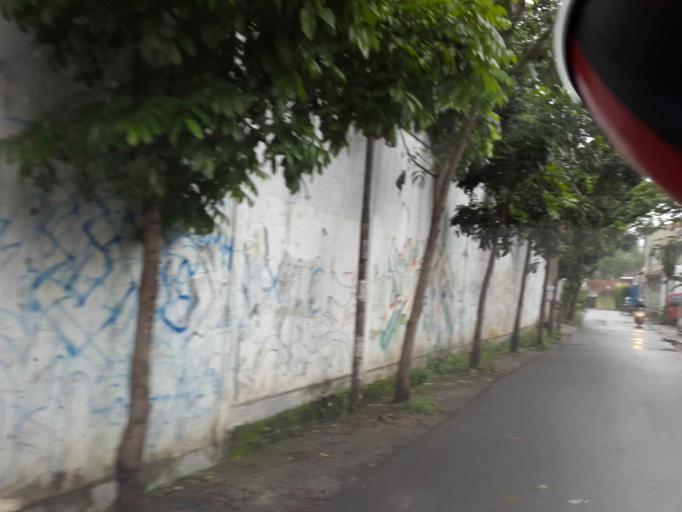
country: ID
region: West Java
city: Cimahi
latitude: -6.8700
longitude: 107.5694
